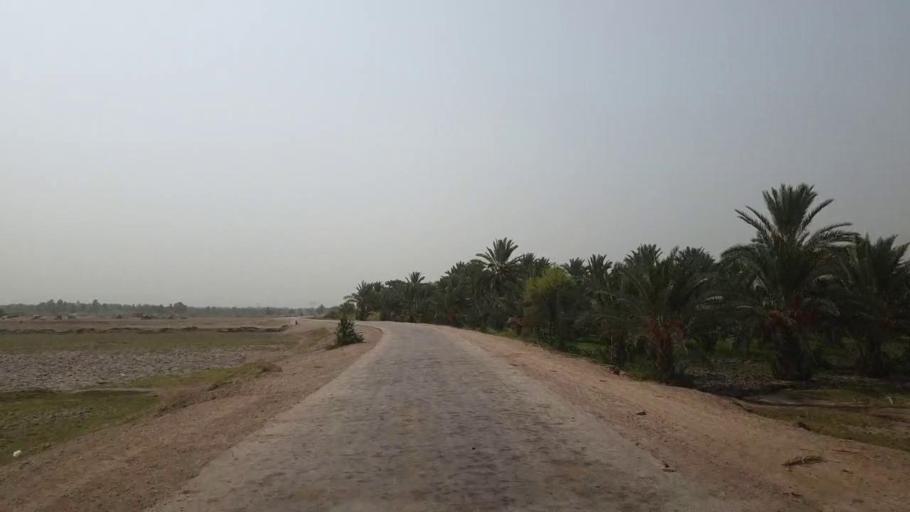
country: PK
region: Sindh
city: Gambat
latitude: 27.4247
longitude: 68.5420
